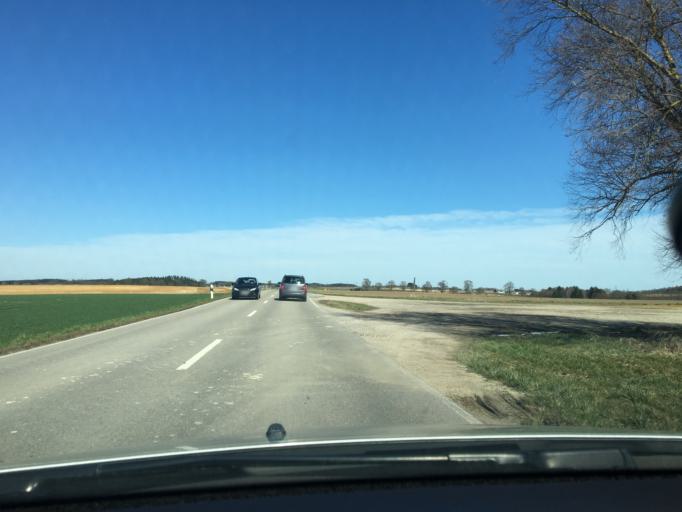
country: DE
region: Bavaria
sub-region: Upper Bavaria
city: Haimhausen
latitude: 48.3219
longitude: 11.5632
